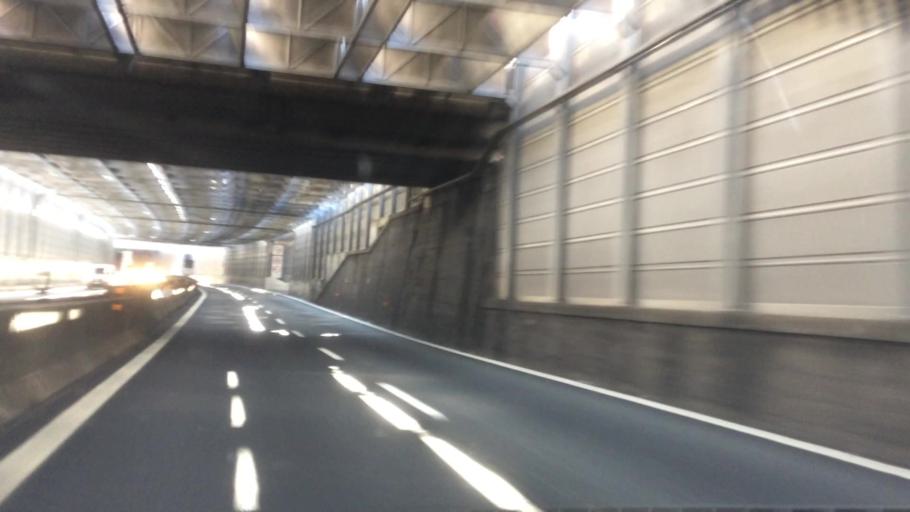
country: IT
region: Liguria
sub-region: Provincia di Genova
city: San Teodoro
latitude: 44.4303
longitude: 8.8448
